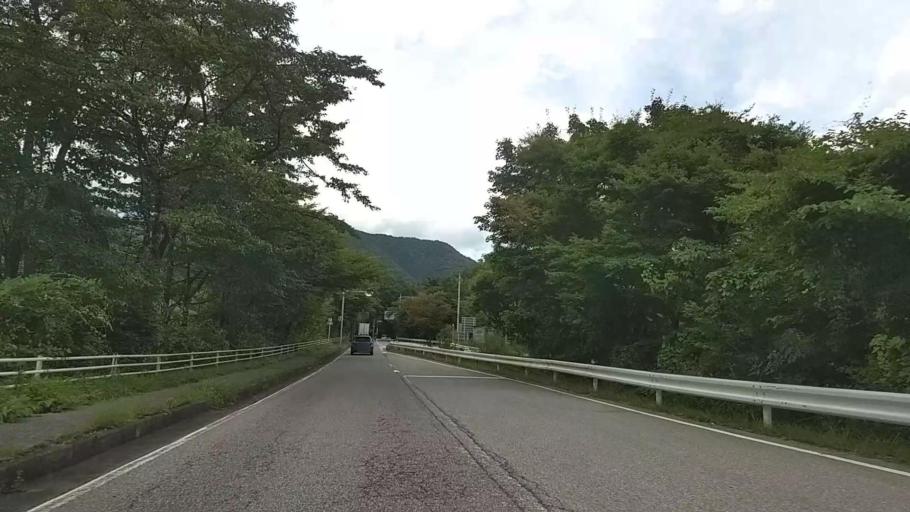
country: JP
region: Tochigi
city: Nikko
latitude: 36.7417
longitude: 139.5665
